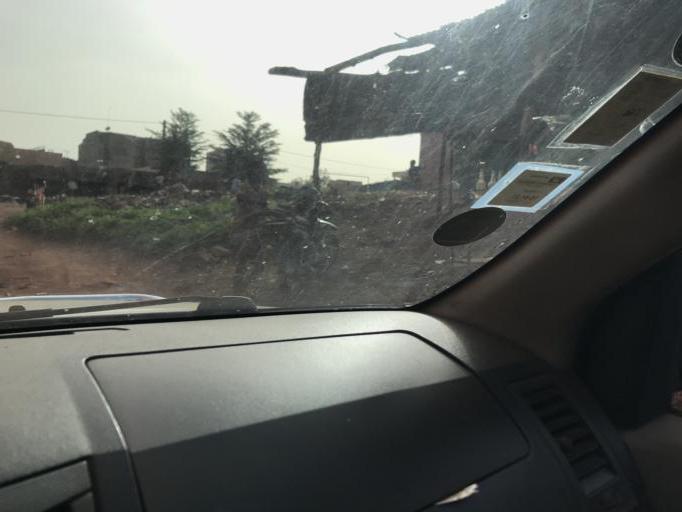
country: ML
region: Bamako
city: Bamako
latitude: 12.5815
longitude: -8.0022
